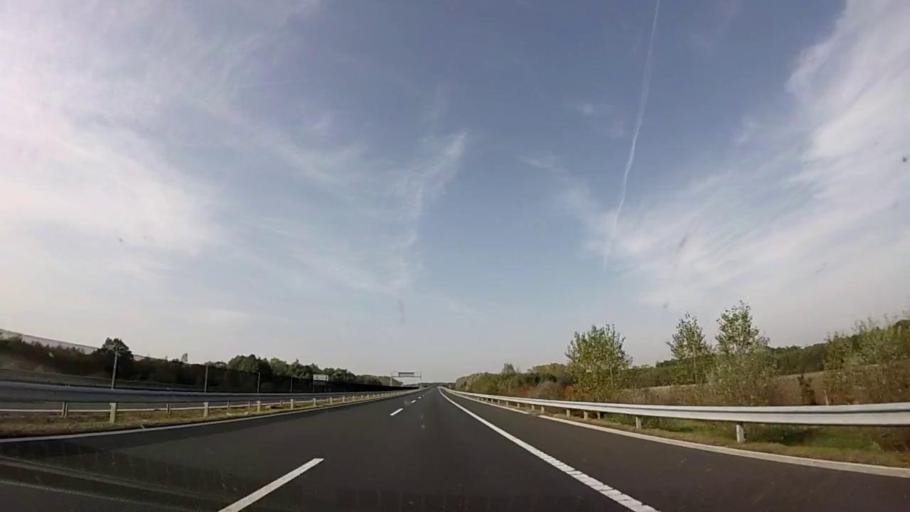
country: HU
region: Zala
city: Zalakomar
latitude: 46.5064
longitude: 17.1696
